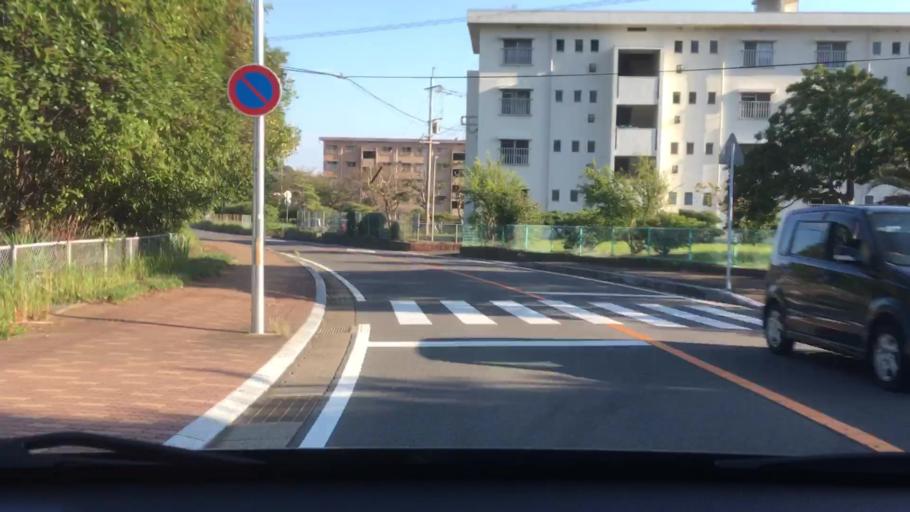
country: JP
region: Nagasaki
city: Sasebo
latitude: 33.0389
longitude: 129.6243
